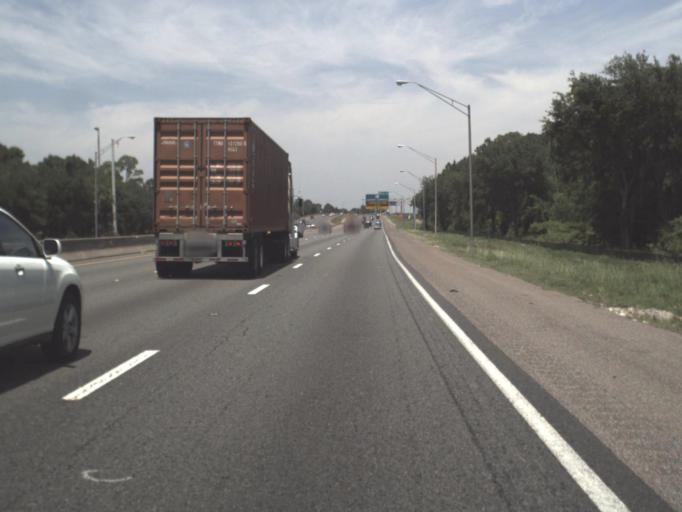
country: US
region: Florida
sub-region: Duval County
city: Jacksonville
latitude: 30.3952
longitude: -81.5614
